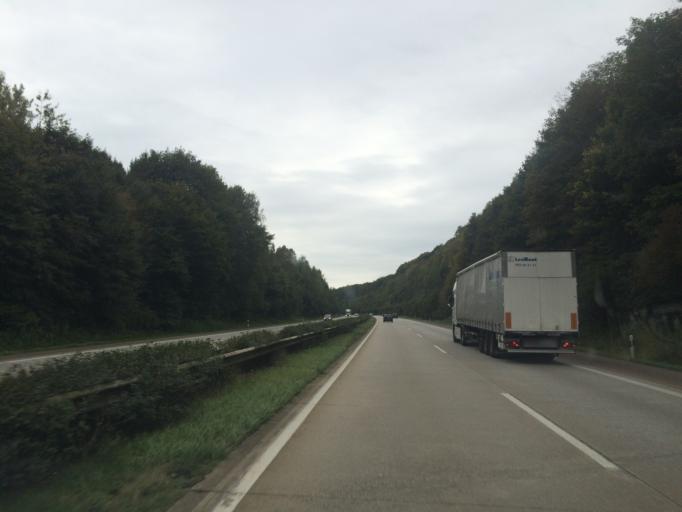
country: DE
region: Rheinland-Pfalz
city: Wittlich
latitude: 49.9682
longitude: 6.8944
